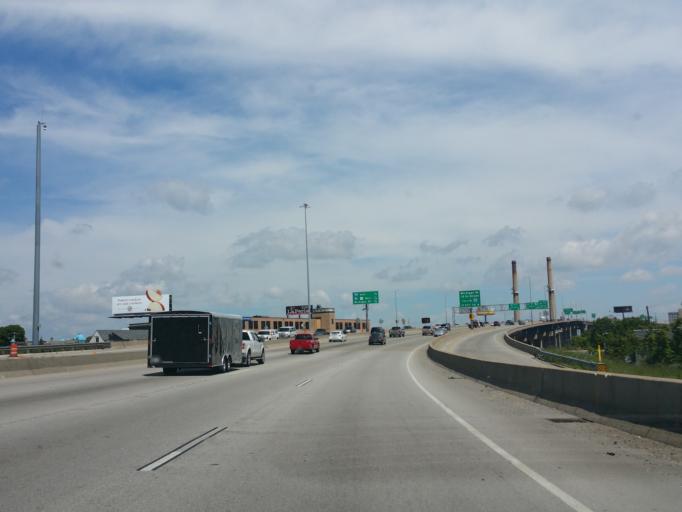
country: US
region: Wisconsin
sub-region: Milwaukee County
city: Milwaukee
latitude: 43.0220
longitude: -87.9200
